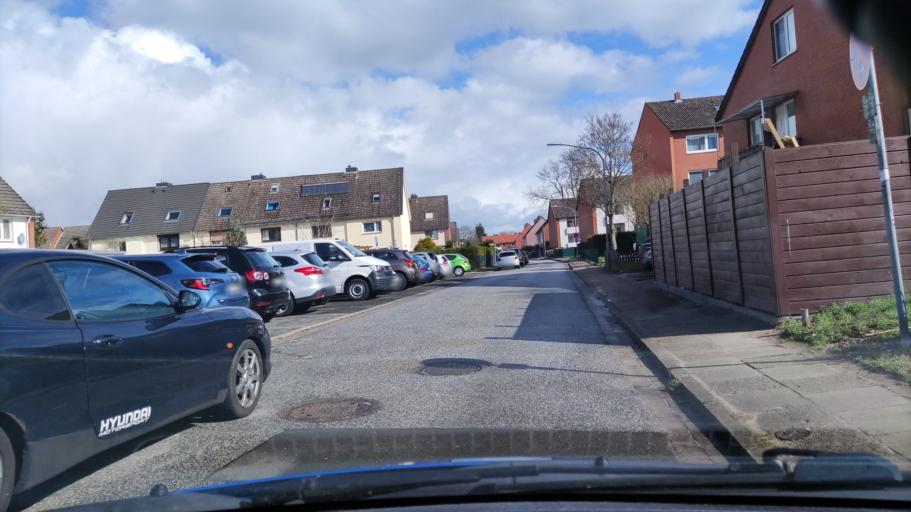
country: DE
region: Lower Saxony
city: Winsen
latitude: 53.3665
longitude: 10.1905
